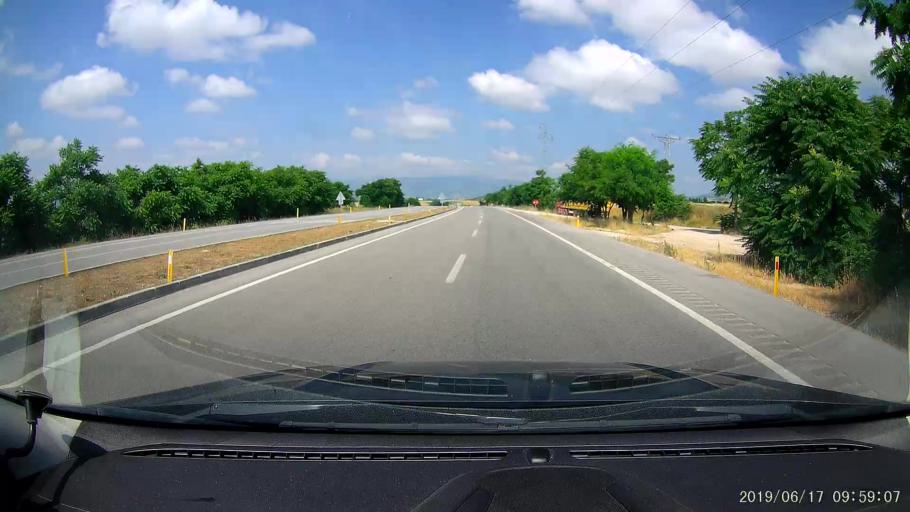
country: TR
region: Amasya
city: Alicik
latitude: 40.8682
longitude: 35.3230
